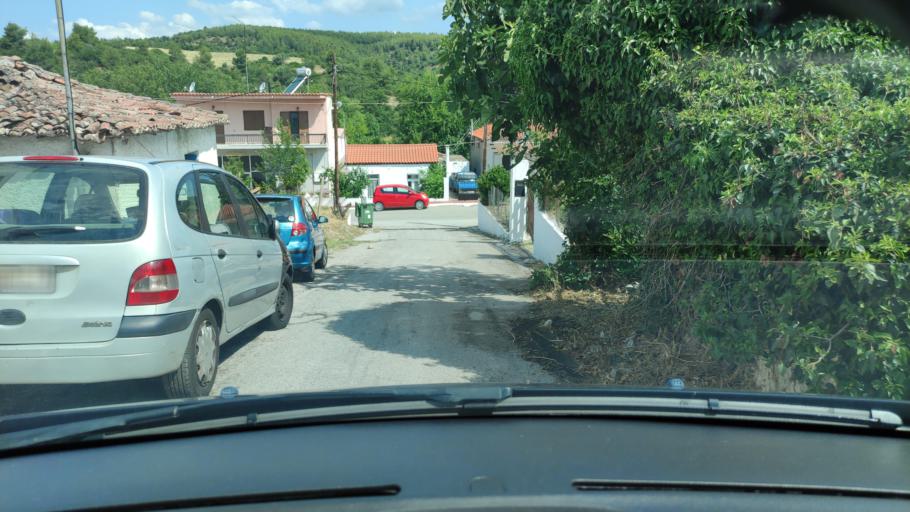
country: GR
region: Central Greece
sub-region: Nomos Evvoias
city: Magoula
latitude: 38.5136
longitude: 23.7800
